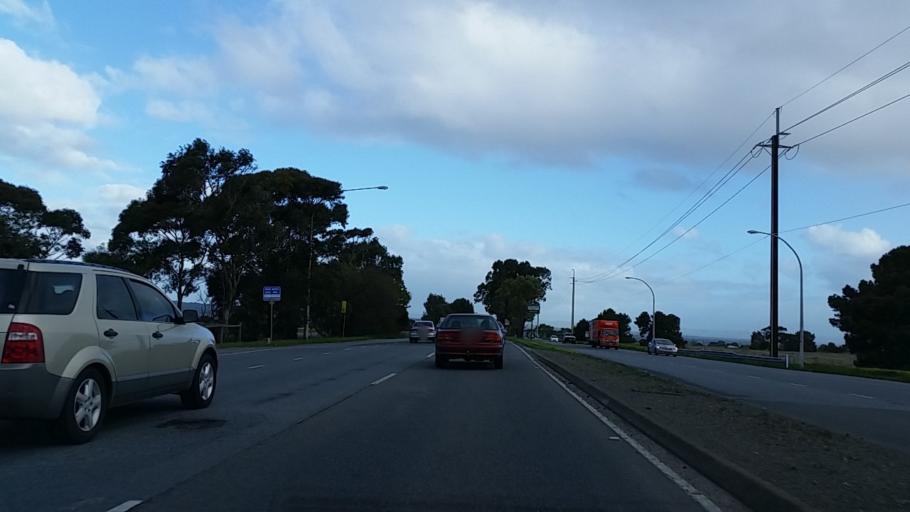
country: AU
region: South Australia
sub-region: Marion
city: Trott Park
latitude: -35.0557
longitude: 138.5351
